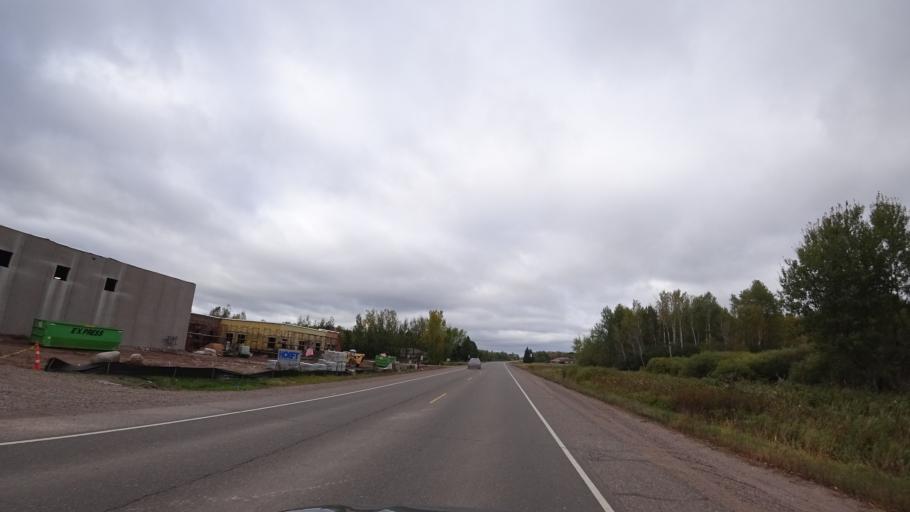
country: US
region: Wisconsin
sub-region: Rusk County
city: Ladysmith
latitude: 45.4769
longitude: -91.1111
